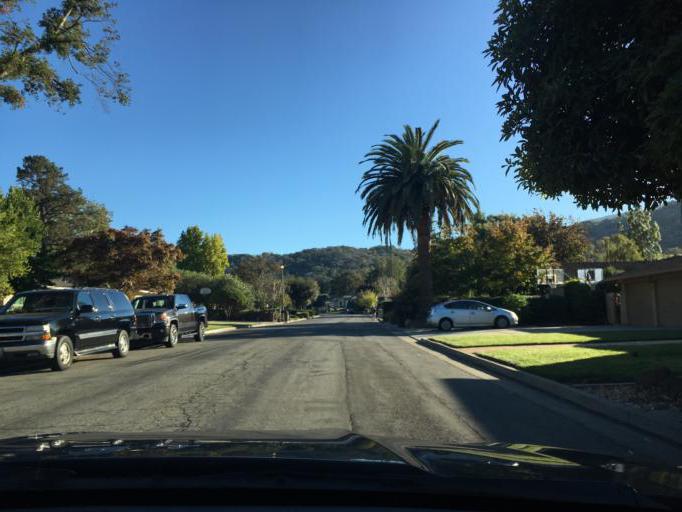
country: US
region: California
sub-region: Santa Clara County
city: Cambrian Park
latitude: 37.2135
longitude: -121.8736
